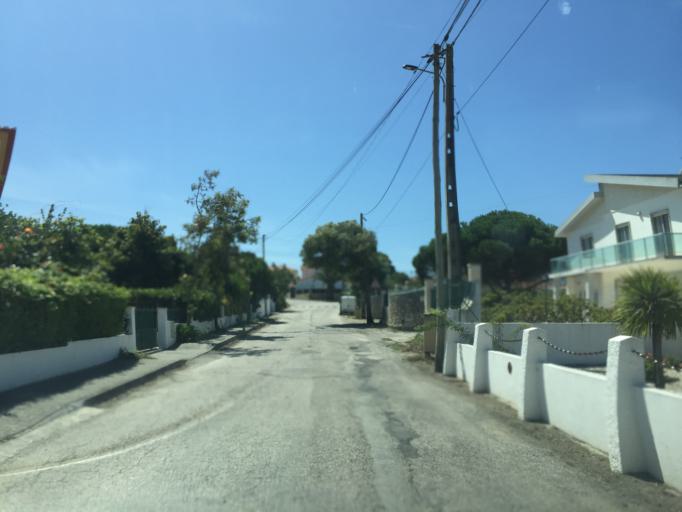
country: PT
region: Lisbon
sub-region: Lourinha
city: Lourinha
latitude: 39.2148
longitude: -9.3217
